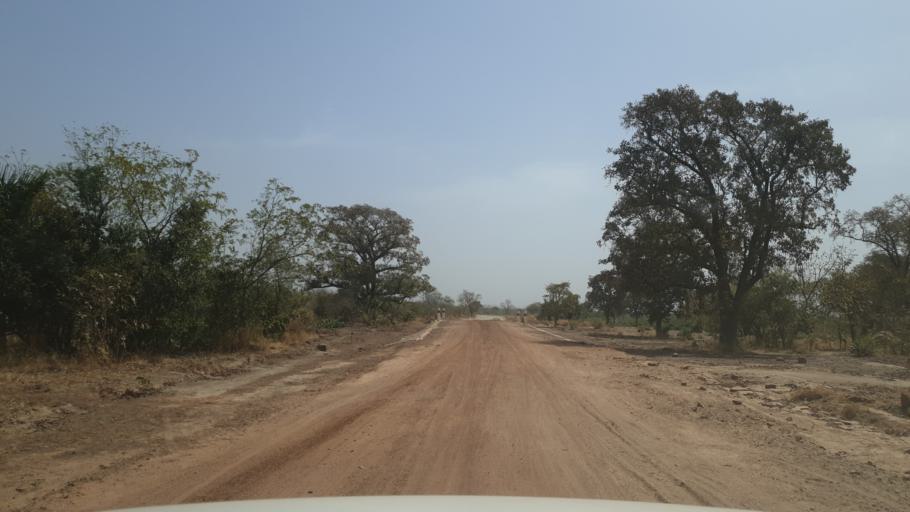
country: ML
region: Koulikoro
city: Kolokani
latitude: 13.5036
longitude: -8.2043
